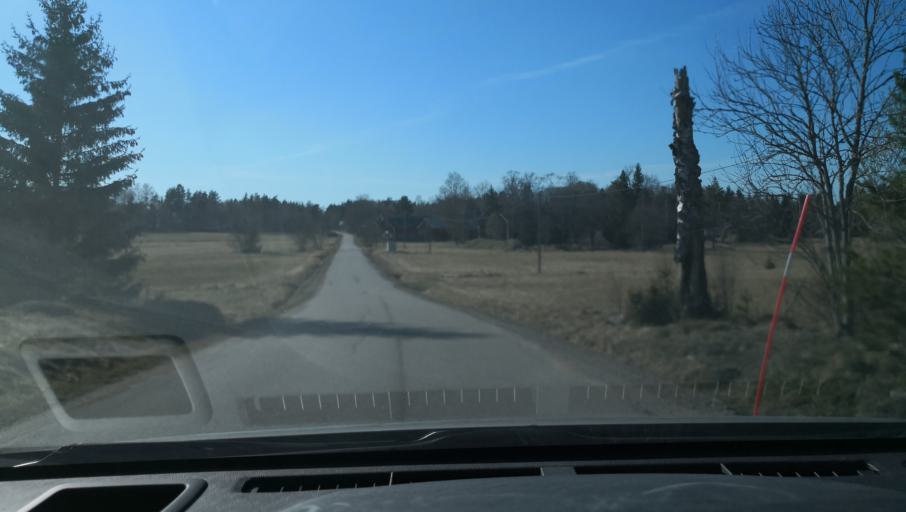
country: SE
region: Vaestmanland
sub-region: Sala Kommun
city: Sala
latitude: 60.0817
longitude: 16.4553
